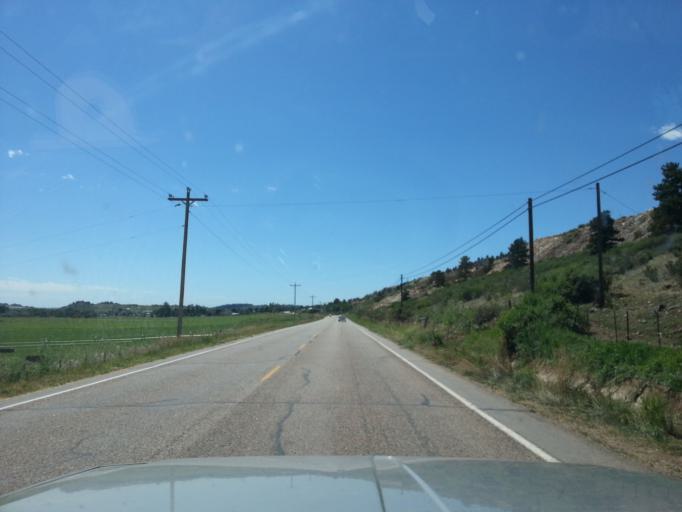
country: US
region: Colorado
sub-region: Larimer County
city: Loveland
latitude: 40.4485
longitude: -105.2036
